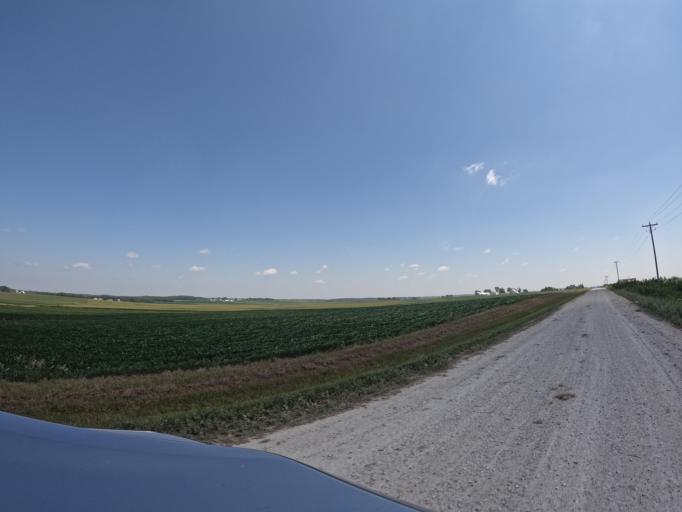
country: US
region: Iowa
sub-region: Keokuk County
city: Sigourney
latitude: 41.2794
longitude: -92.2278
